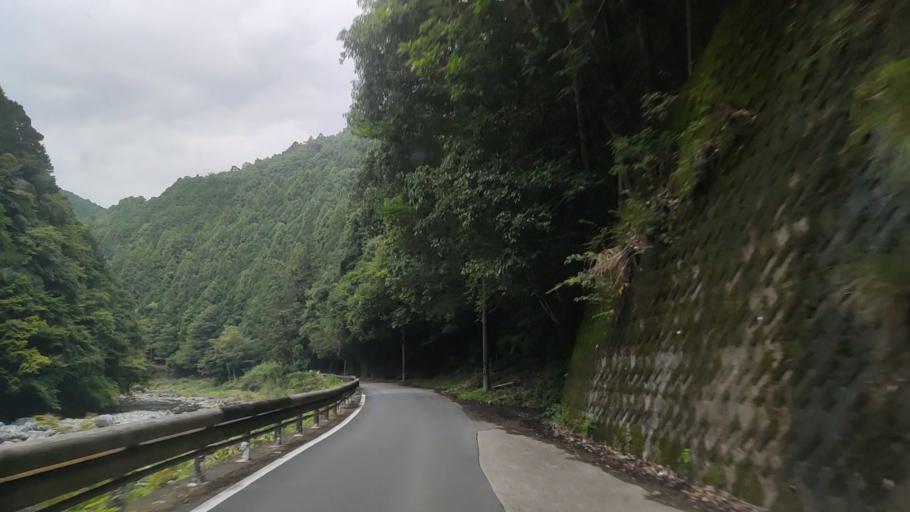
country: JP
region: Wakayama
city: Hashimoto
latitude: 34.2676
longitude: 135.6452
